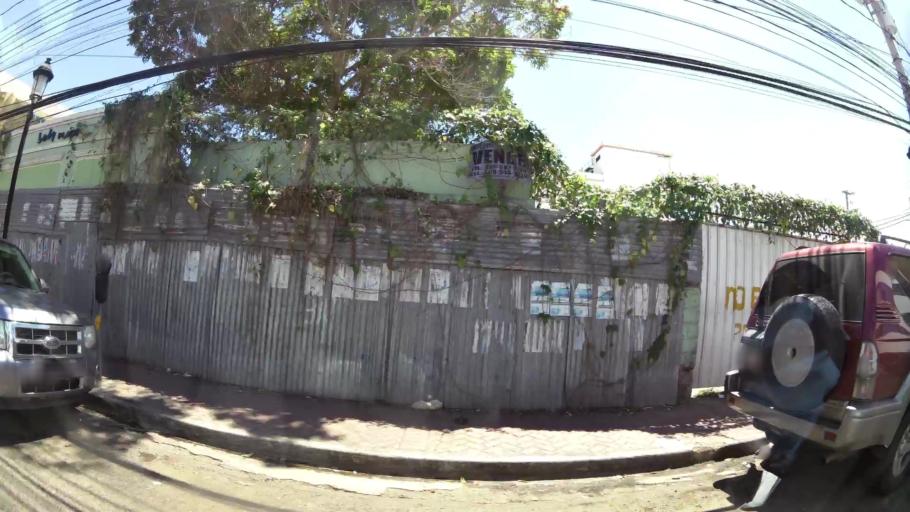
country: DO
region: Santiago
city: Santiago de los Caballeros
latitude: 19.4525
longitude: -70.7025
